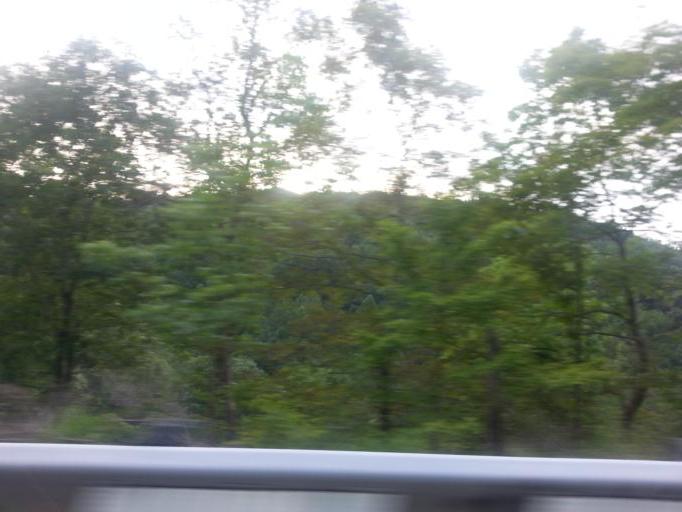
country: US
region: Tennessee
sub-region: Anderson County
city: Clinton
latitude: 36.1287
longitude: -84.2329
